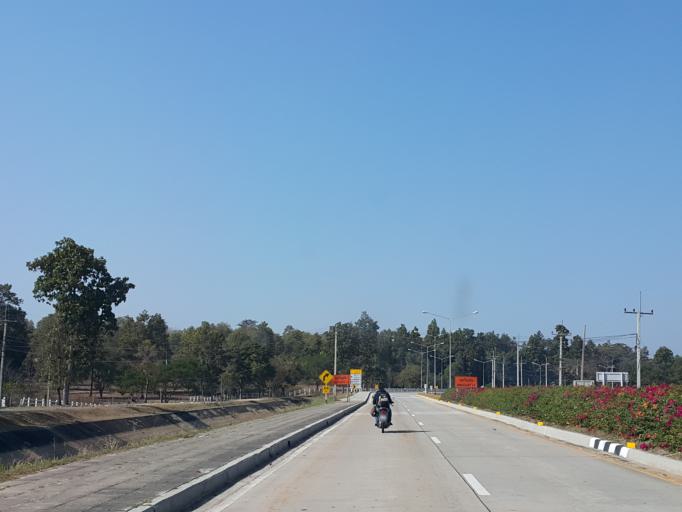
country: TH
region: Chiang Mai
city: Chiang Mai
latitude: 18.8630
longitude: 98.9598
